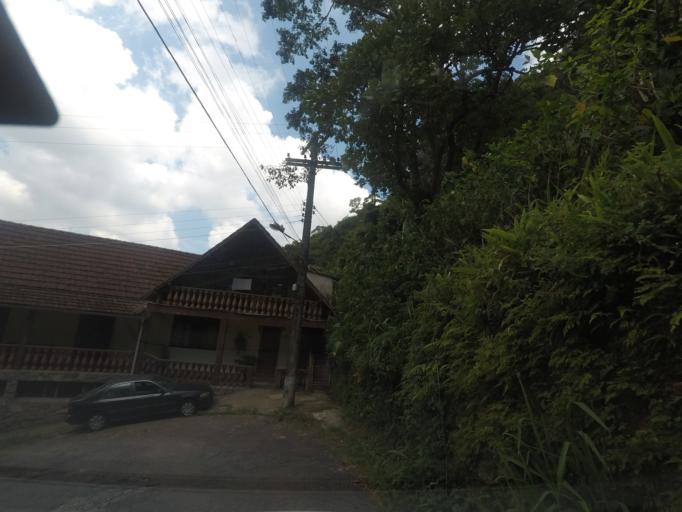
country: BR
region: Rio de Janeiro
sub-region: Petropolis
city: Petropolis
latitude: -22.4980
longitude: -43.1891
